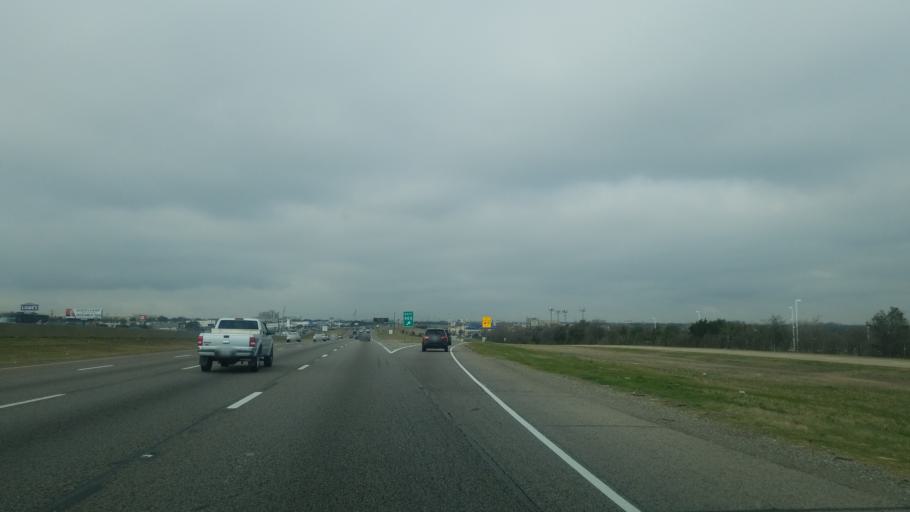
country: US
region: Texas
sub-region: Dallas County
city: DeSoto
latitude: 32.6450
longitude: -96.8507
